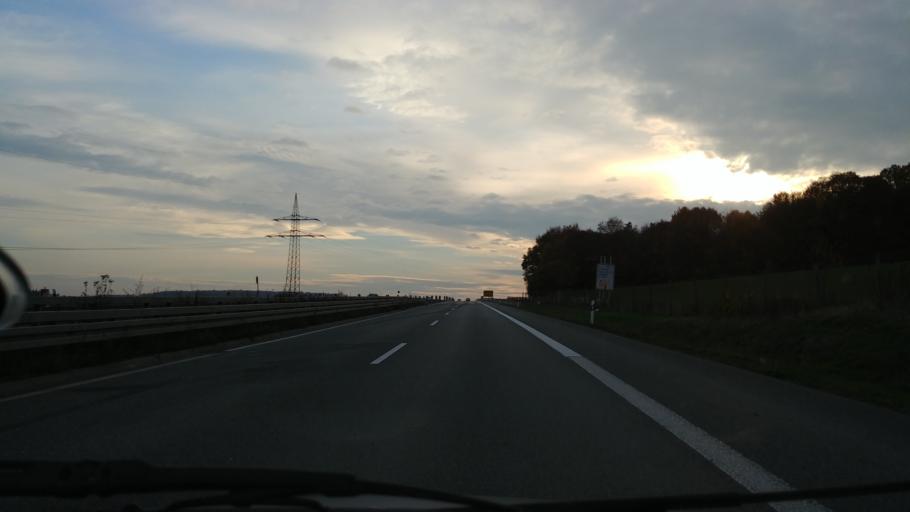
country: DE
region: Hesse
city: Merenberg
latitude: 50.4934
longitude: 8.1765
